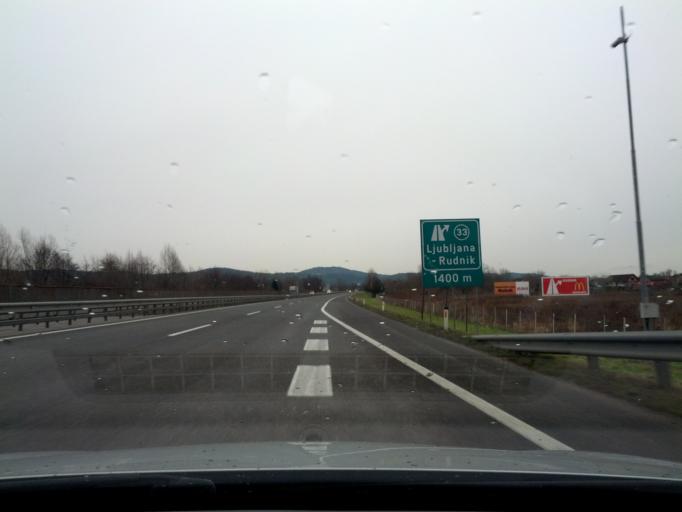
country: SI
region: Ljubljana
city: Ljubljana
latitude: 46.0253
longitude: 14.5008
